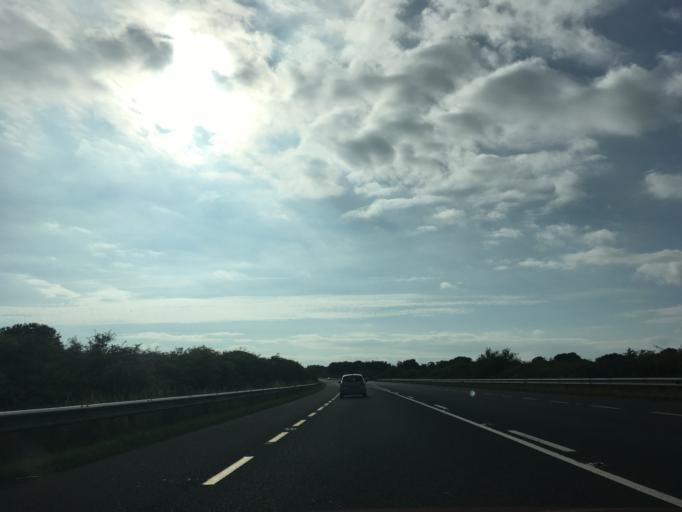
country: IE
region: Leinster
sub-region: Loch Garman
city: Enniscorthy
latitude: 52.3500
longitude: -6.6317
